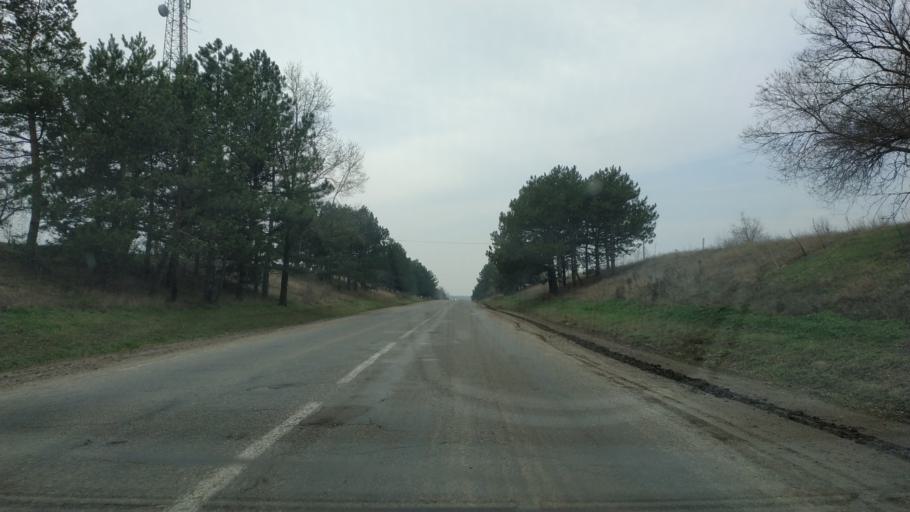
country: MD
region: Cahul
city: Cahul
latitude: 45.9332
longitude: 28.2775
